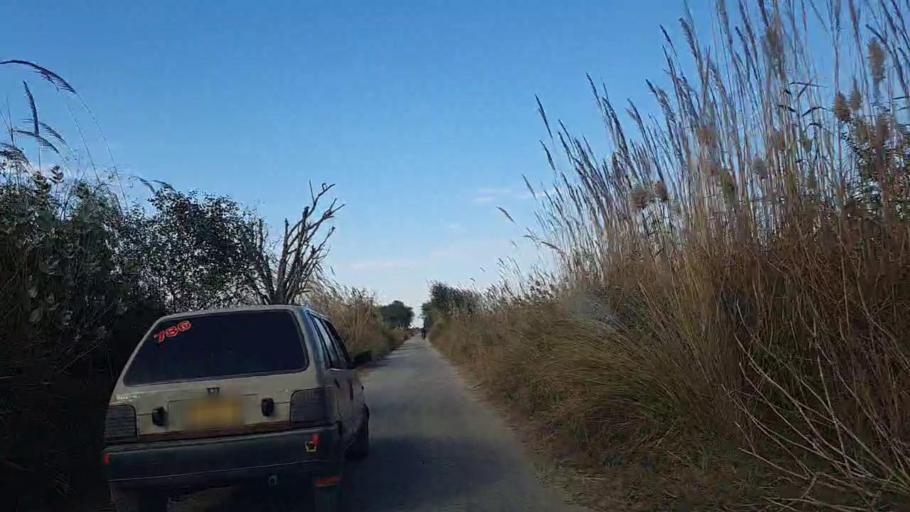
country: PK
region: Sindh
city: Khadro
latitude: 26.2818
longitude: 68.8200
